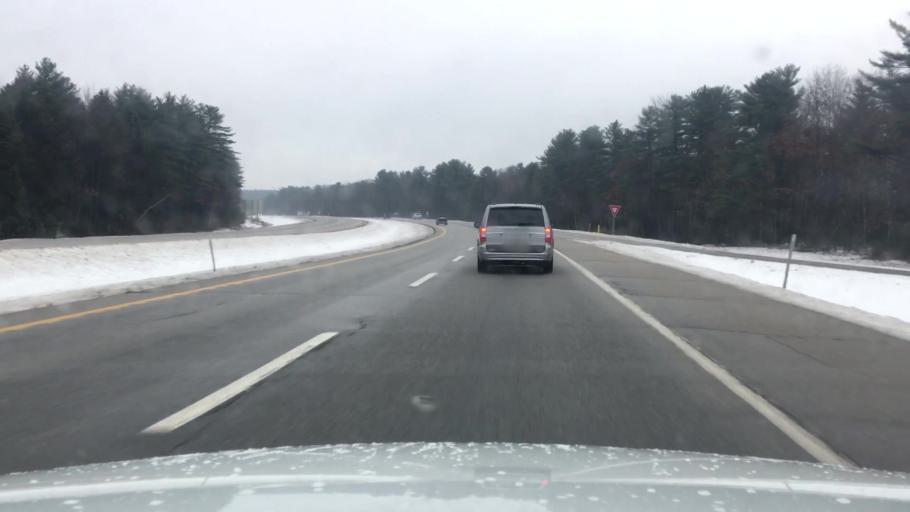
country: US
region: Maine
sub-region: Cumberland County
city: South Portland Gardens
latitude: 43.6211
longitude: -70.3210
